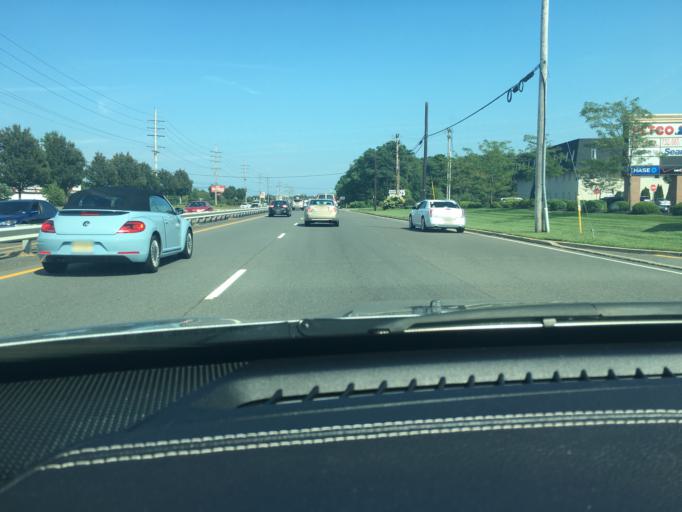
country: US
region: New Jersey
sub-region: Ocean County
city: Leisure Village East
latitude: 40.0567
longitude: -74.1536
